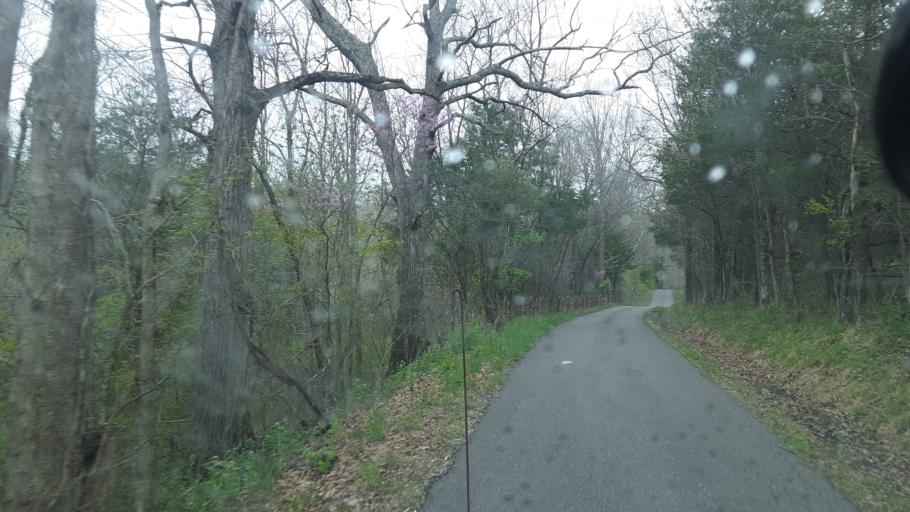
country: US
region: Kentucky
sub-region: Owen County
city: Owenton
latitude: 38.6468
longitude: -84.7886
